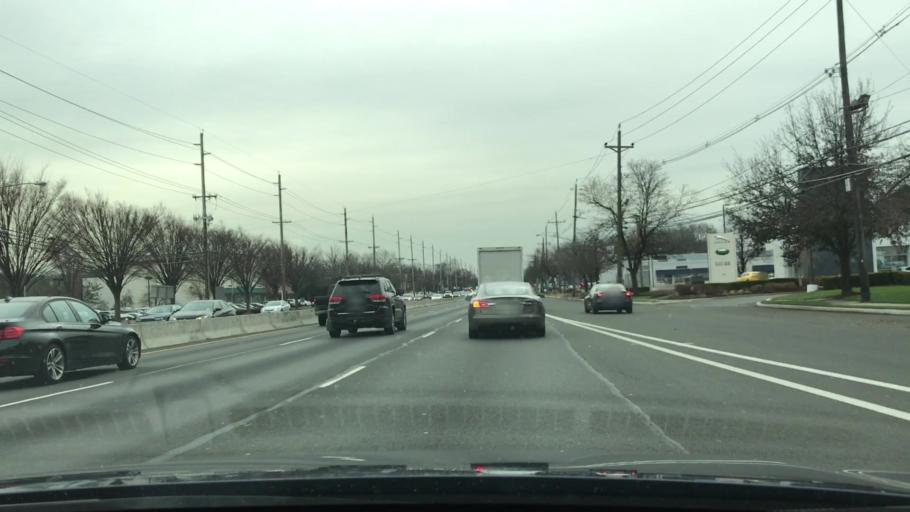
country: US
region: New Jersey
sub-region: Bergen County
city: Paramus
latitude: 40.9490
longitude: -74.0725
